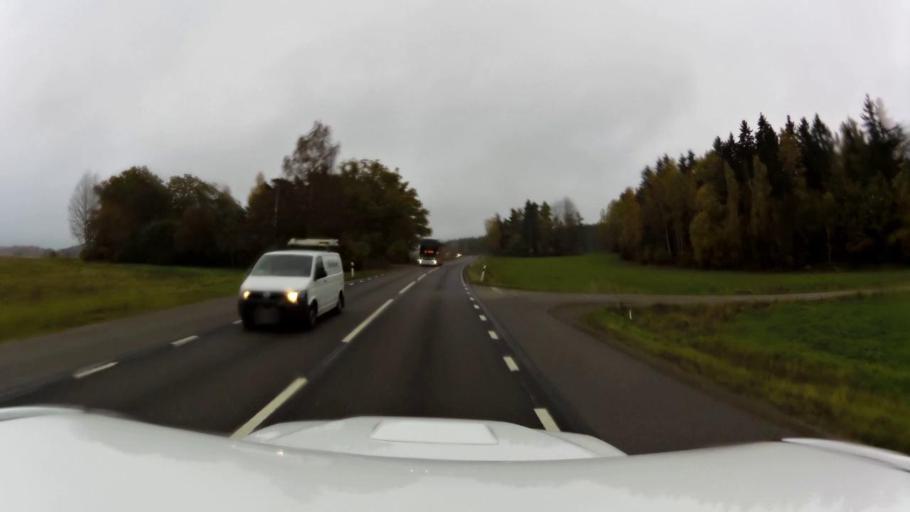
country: SE
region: OEstergoetland
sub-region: Linkopings Kommun
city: Linghem
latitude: 58.3685
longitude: 15.8191
